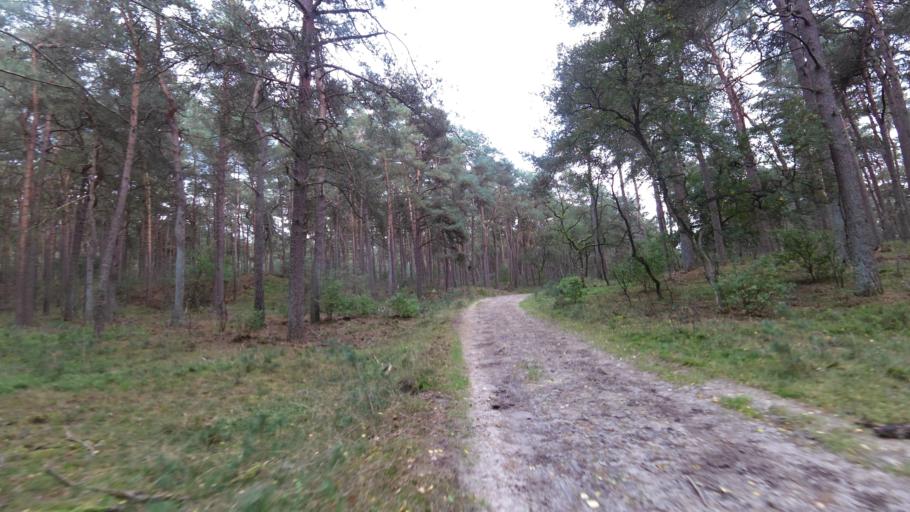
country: NL
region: Gelderland
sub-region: Gemeente Ede
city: Harskamp
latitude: 52.1700
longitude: 5.7417
